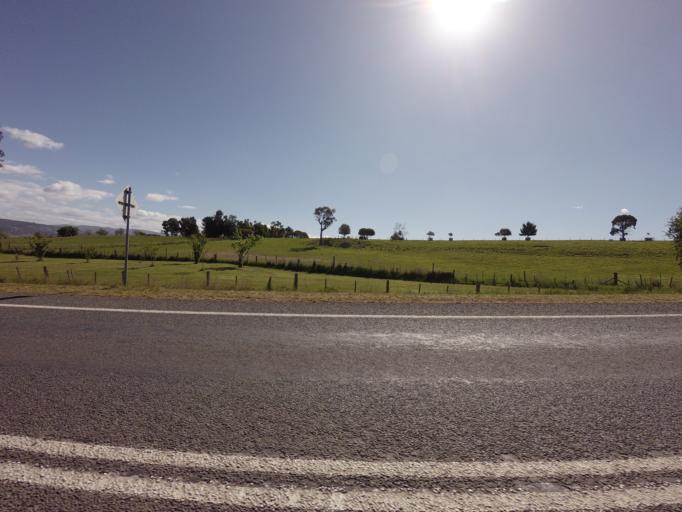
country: AU
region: Tasmania
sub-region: Derwent Valley
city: New Norfolk
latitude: -42.7006
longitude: 146.9421
